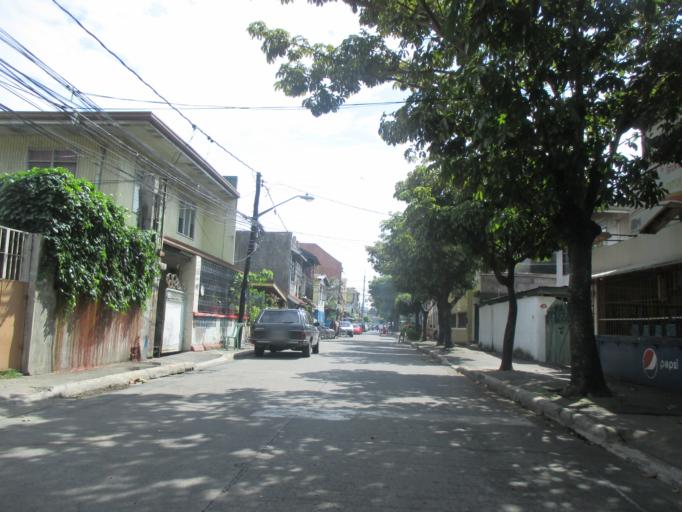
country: PH
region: Metro Manila
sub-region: Marikina
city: Calumpang
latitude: 14.6224
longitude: 121.0911
